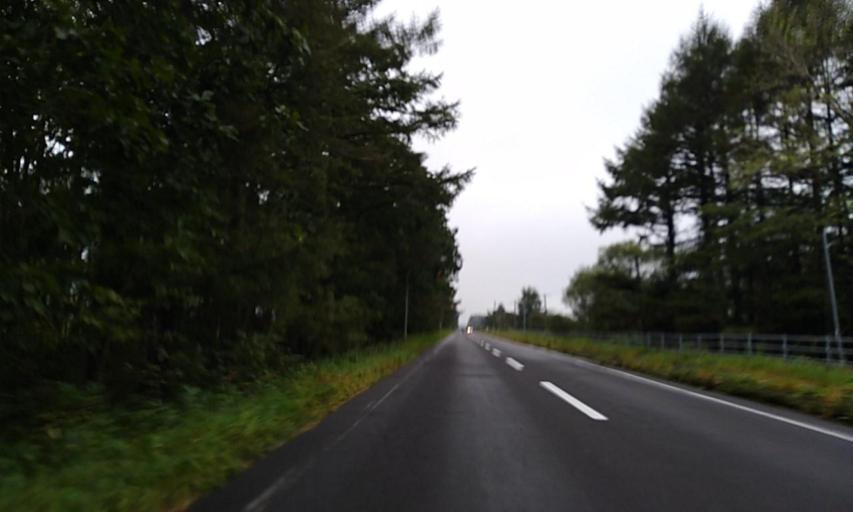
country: JP
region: Hokkaido
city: Shibetsu
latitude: 43.4958
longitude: 144.6481
